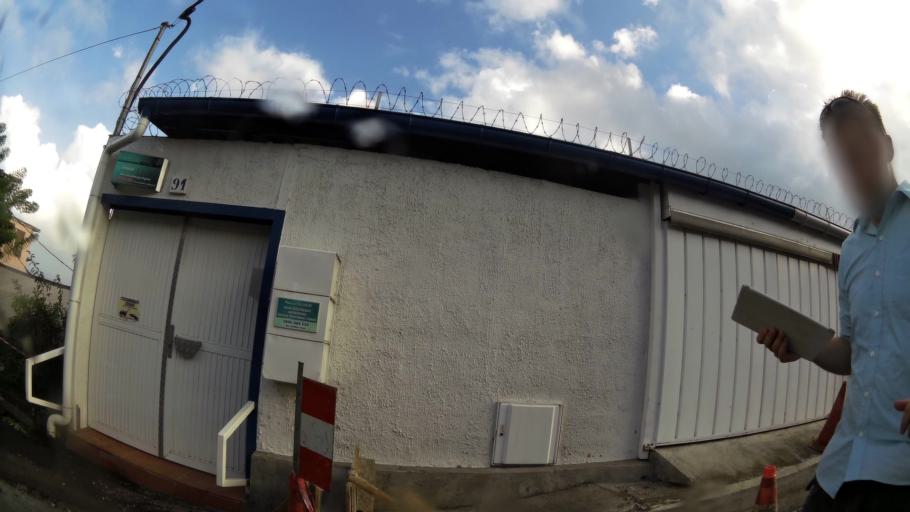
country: MQ
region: Martinique
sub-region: Martinique
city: Fort-de-France
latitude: 14.6043
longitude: -61.0766
